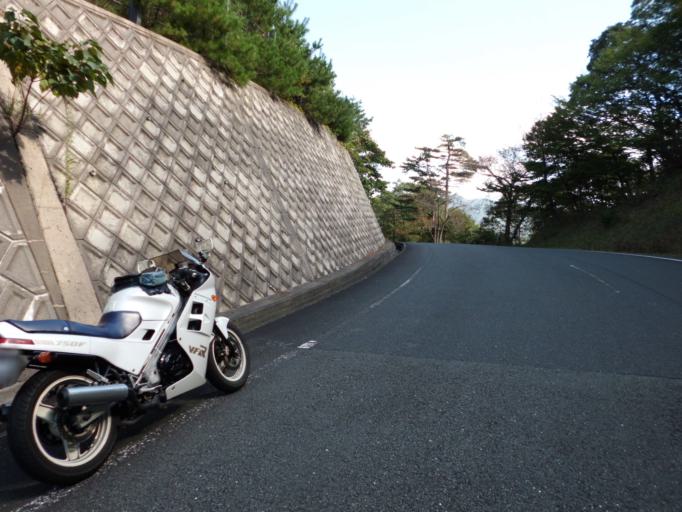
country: JP
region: Hyogo
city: Toyooka
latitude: 35.5366
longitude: 134.9182
